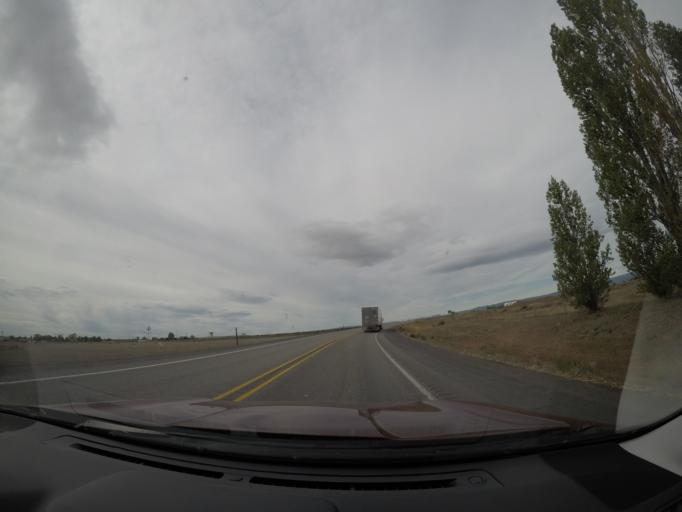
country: US
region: Washington
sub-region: Grant County
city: Quincy
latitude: 47.0925
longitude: -119.8553
